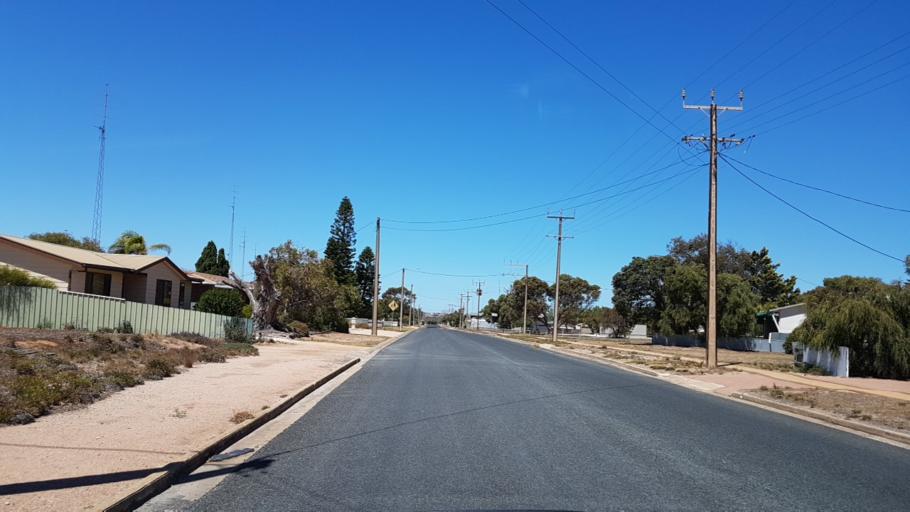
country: AU
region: South Australia
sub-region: Copper Coast
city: Wallaroo
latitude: -33.8995
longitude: 137.6305
